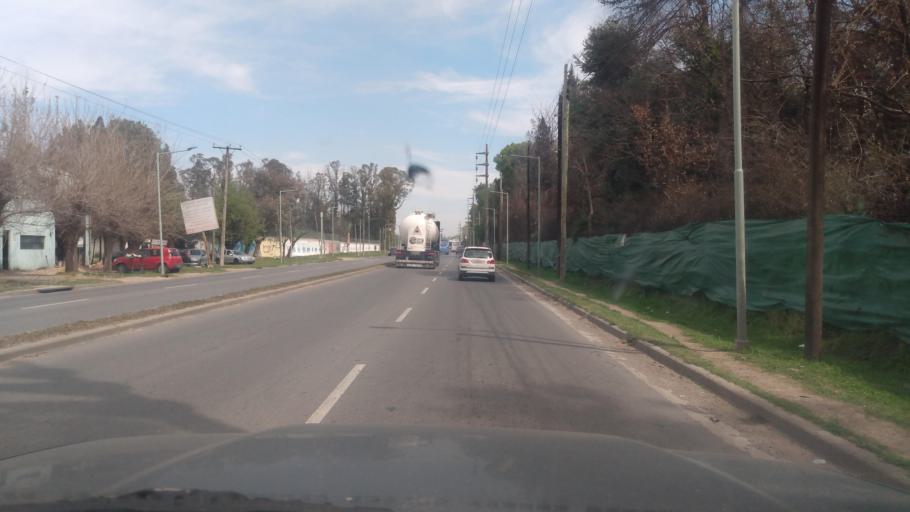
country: AR
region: Buenos Aires
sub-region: Partido de Pilar
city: Pilar
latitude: -34.4400
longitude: -58.8968
